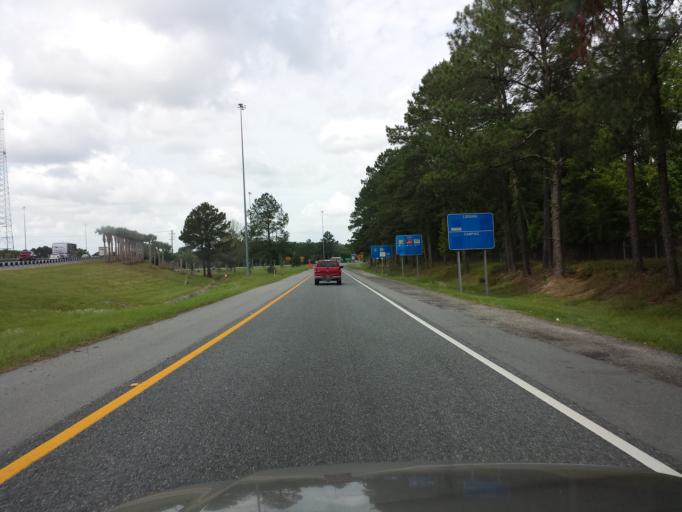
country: US
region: Florida
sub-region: Alachua County
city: High Springs
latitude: 29.9989
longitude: -82.5939
